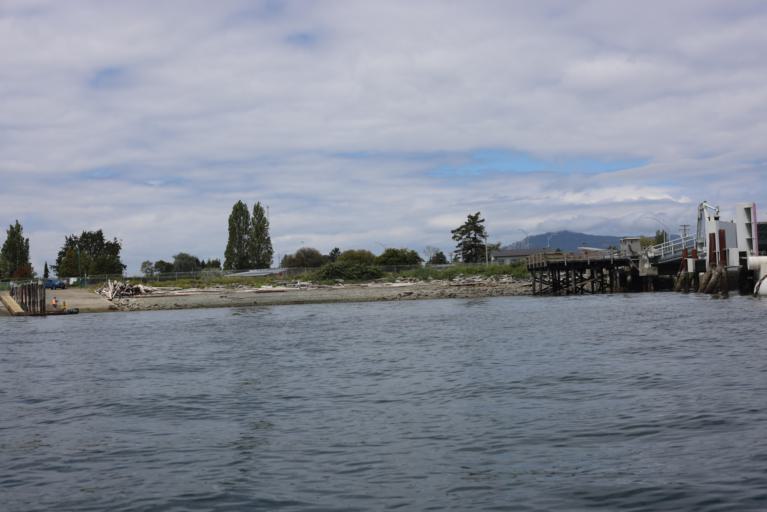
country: CA
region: British Columbia
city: North Saanich
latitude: 48.6422
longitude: -123.3960
